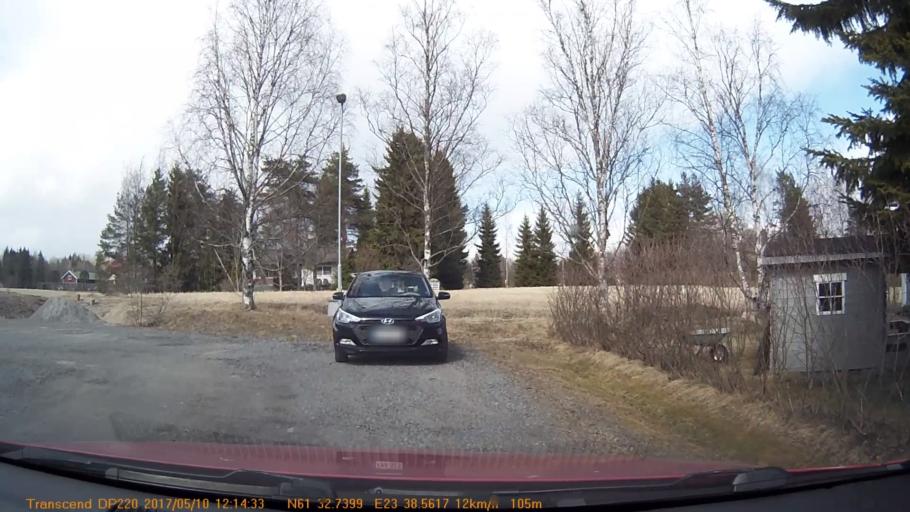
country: FI
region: Pirkanmaa
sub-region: Tampere
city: Yloejaervi
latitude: 61.5457
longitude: 23.6430
